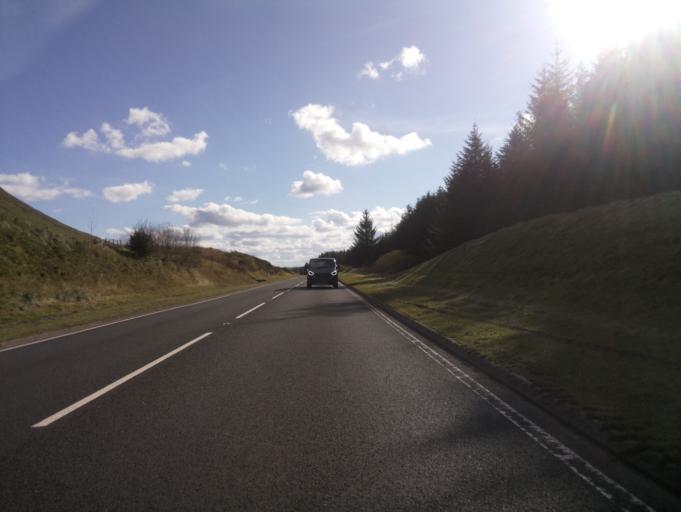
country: GB
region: Wales
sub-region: Sir Powys
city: Brecon
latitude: 51.8630
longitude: -3.4714
